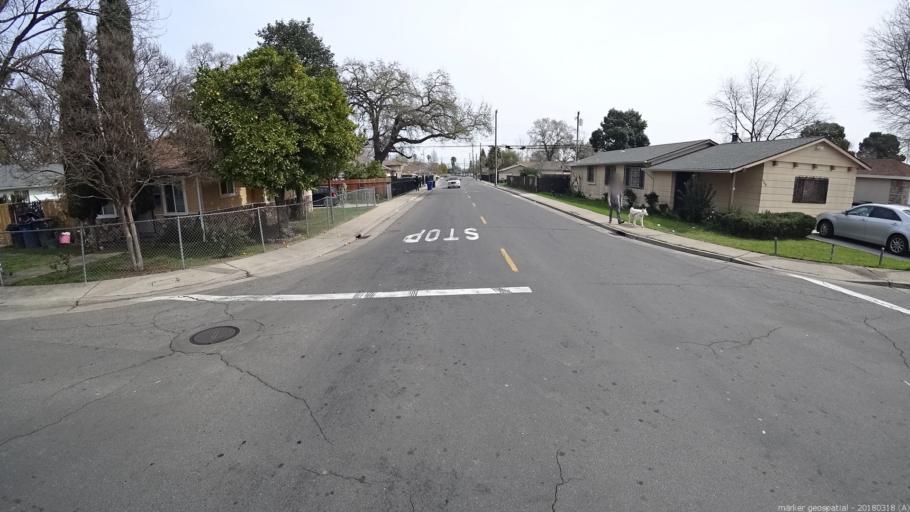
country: US
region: California
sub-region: Sacramento County
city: Parkway
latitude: 38.5197
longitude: -121.4490
